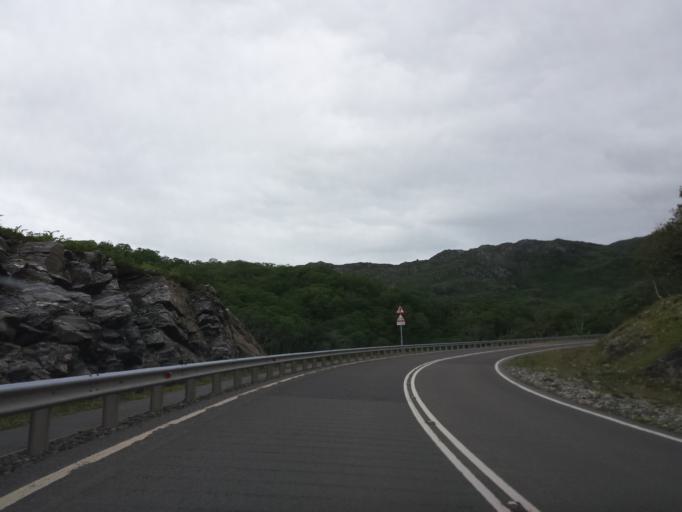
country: GB
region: Scotland
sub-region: Argyll and Bute
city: Isle Of Mull
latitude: 56.8946
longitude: -5.7578
